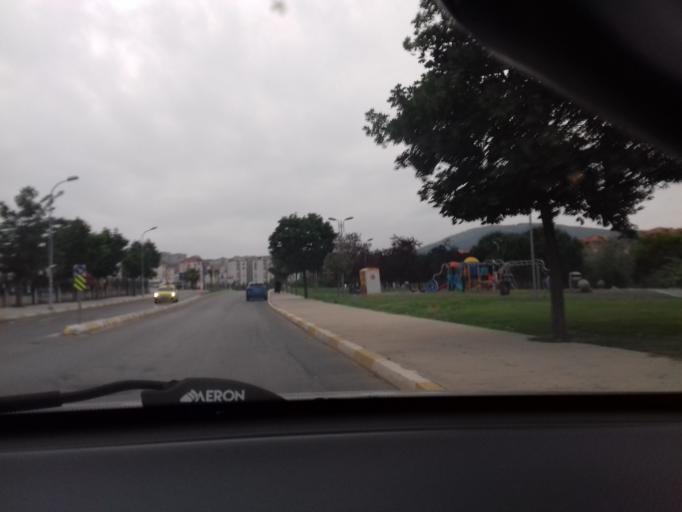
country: TR
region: Istanbul
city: Sultanbeyli
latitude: 40.9268
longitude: 29.2926
